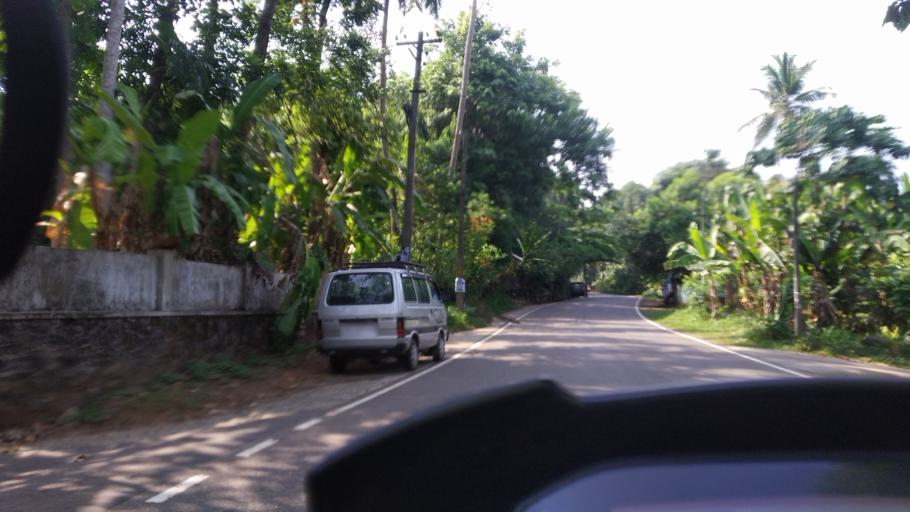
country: IN
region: Kerala
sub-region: Ernakulam
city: Piravam
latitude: 9.8239
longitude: 76.5491
